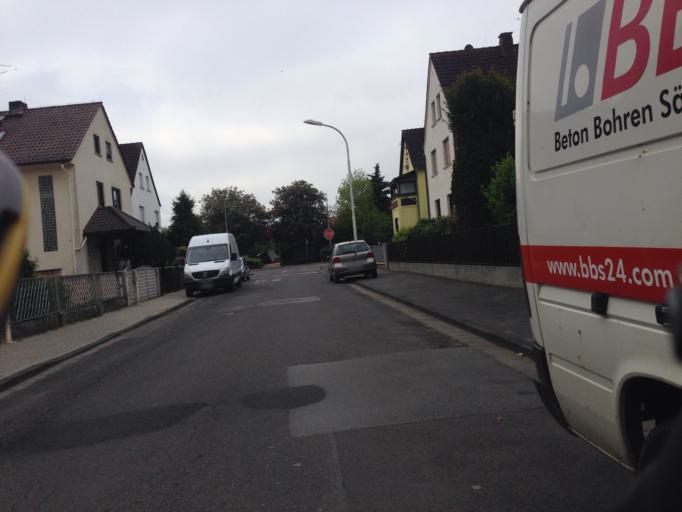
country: DE
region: Hesse
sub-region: Regierungsbezirk Darmstadt
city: Rodgau
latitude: 50.0514
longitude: 8.8883
